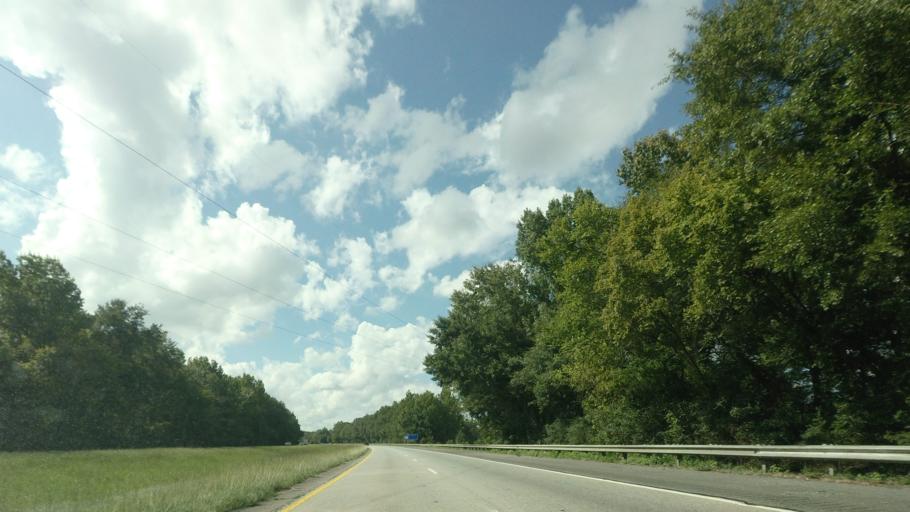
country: US
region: Georgia
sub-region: Bibb County
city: Macon
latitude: 32.8123
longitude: -83.5780
